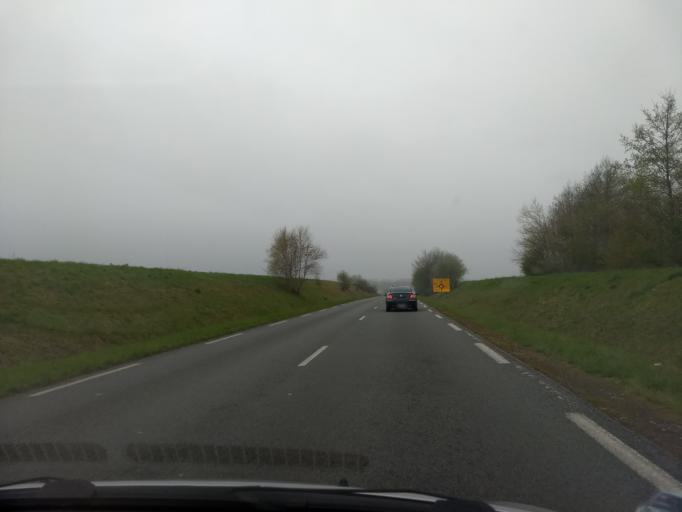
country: FR
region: Nord-Pas-de-Calais
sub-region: Departement du Pas-de-Calais
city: Verton
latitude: 50.4126
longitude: 1.6615
